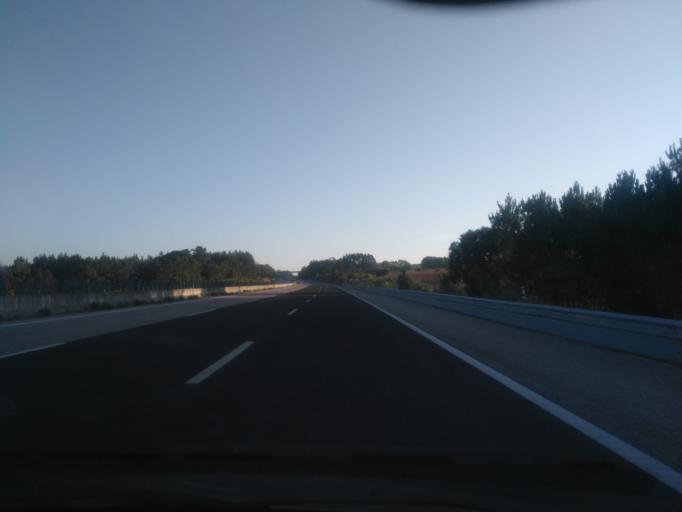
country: PT
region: Coimbra
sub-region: Figueira da Foz
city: Lavos
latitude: 40.0906
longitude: -8.7619
